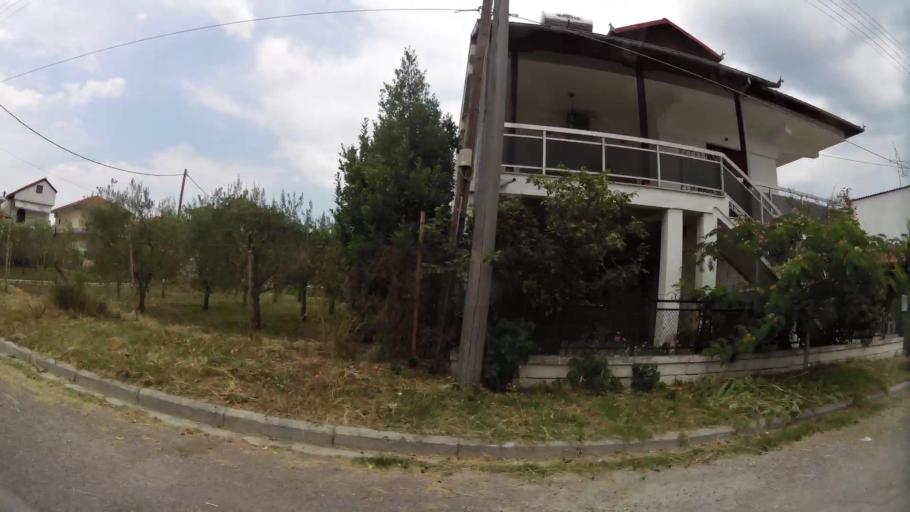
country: GR
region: Central Macedonia
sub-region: Nomos Pierias
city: Kallithea
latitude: 40.2719
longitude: 22.5771
